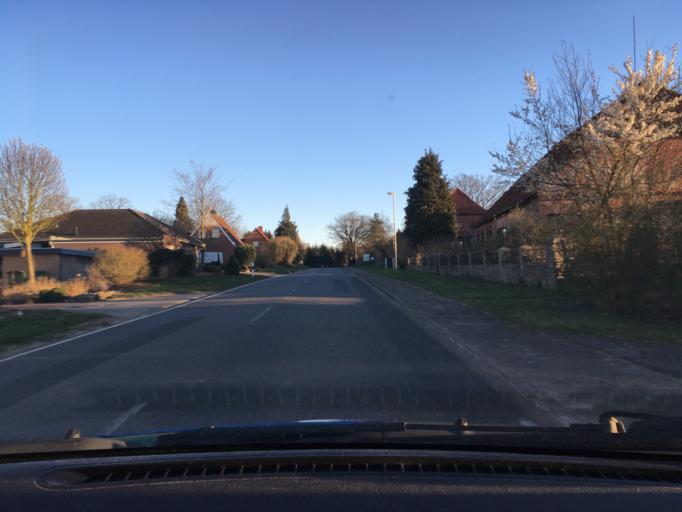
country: DE
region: Lower Saxony
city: Dahlem
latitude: 53.2161
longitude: 10.7551
